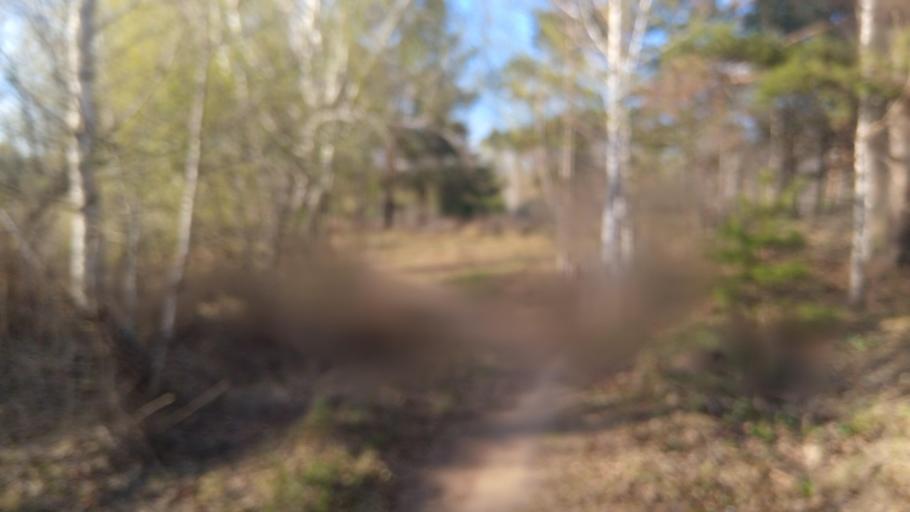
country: RU
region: Chelyabinsk
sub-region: Gorod Chelyabinsk
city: Chelyabinsk
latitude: 55.1551
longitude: 61.3229
